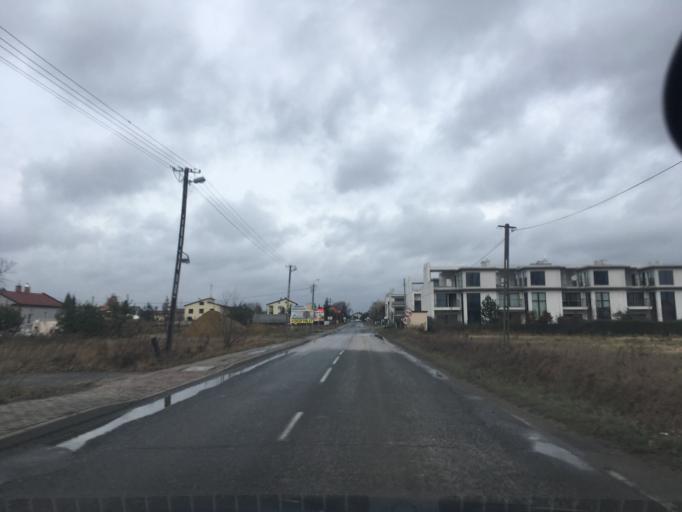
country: PL
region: Masovian Voivodeship
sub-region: Powiat piaseczynski
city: Lesznowola
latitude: 52.1010
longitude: 20.9323
